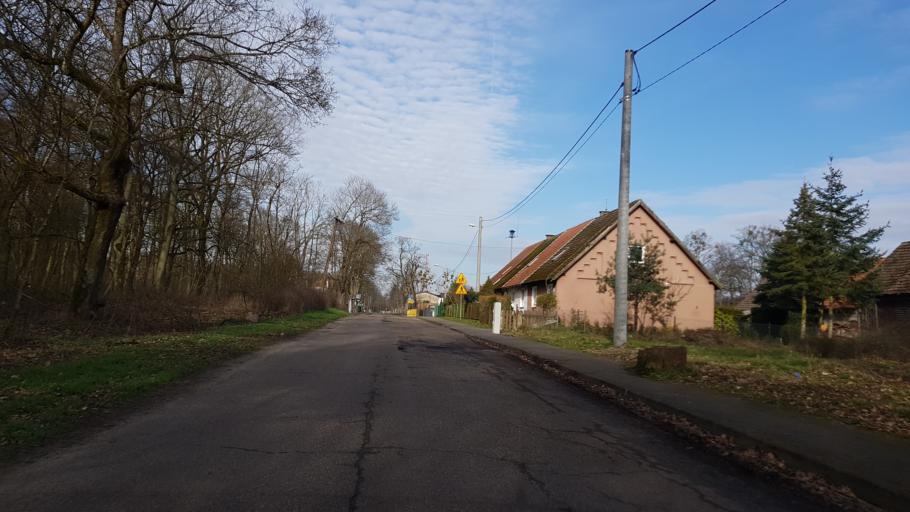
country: PL
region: West Pomeranian Voivodeship
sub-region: Powiat policki
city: Dobra
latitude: 53.5312
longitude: 14.3331
